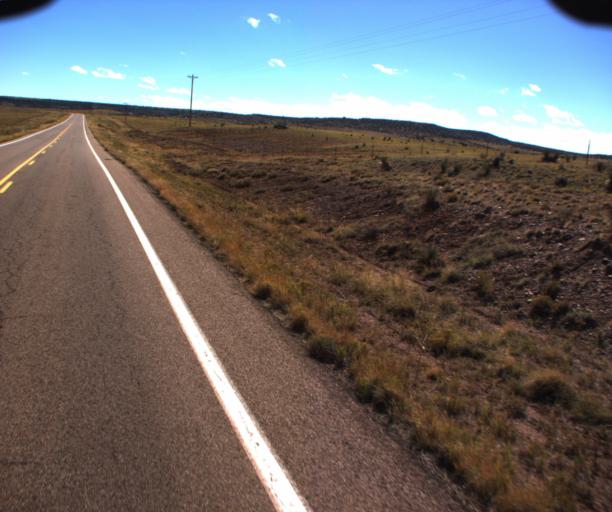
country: US
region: Arizona
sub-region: Apache County
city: Saint Johns
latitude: 34.4890
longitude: -109.6204
